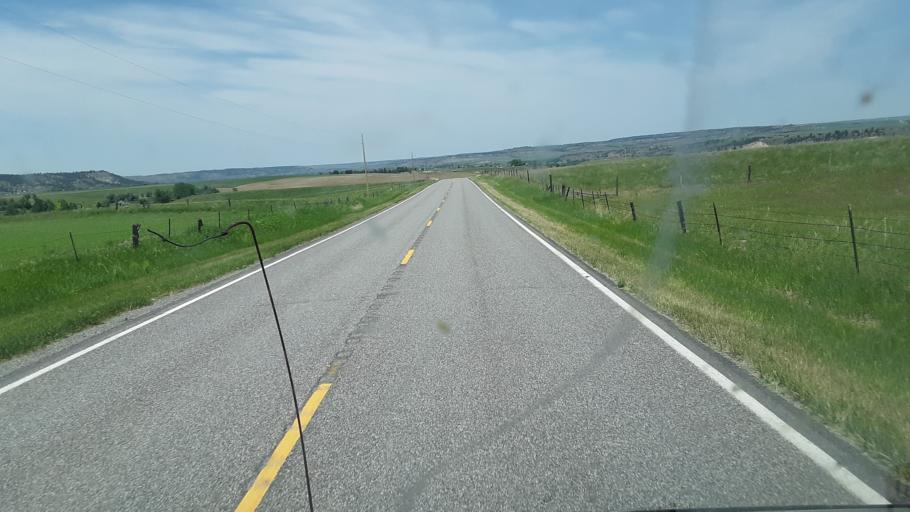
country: US
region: Montana
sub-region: Stillwater County
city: Columbus
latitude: 45.5911
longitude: -109.1936
